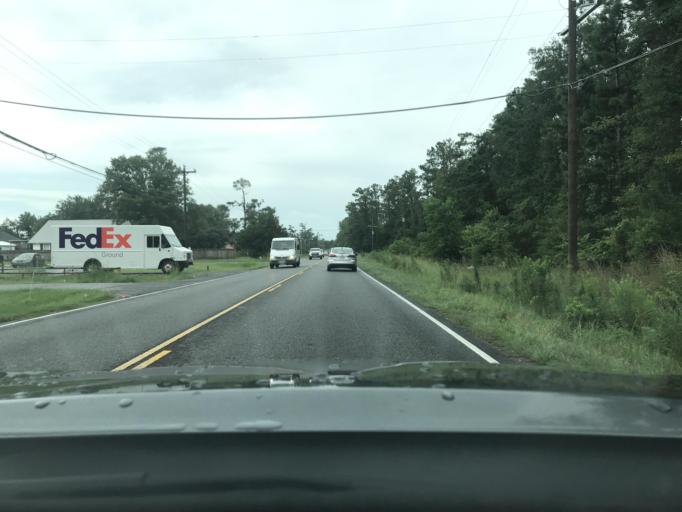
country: US
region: Louisiana
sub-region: Calcasieu Parish
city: Westlake
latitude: 30.2876
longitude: -93.2498
